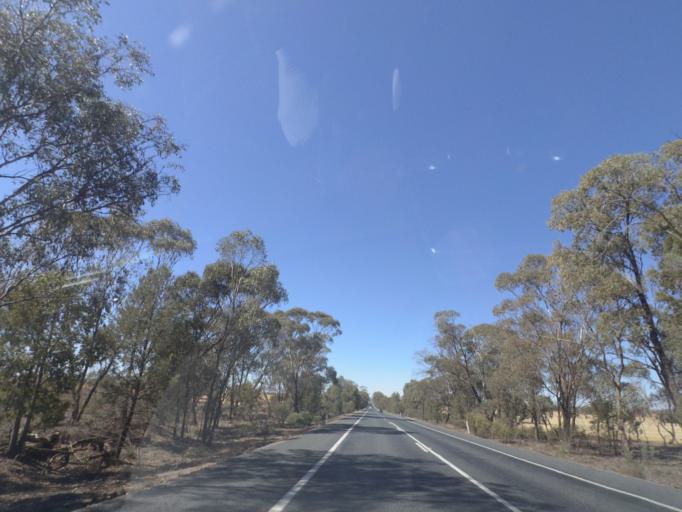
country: AU
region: New South Wales
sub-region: Bland
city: West Wyalong
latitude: -34.1693
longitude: 147.1153
